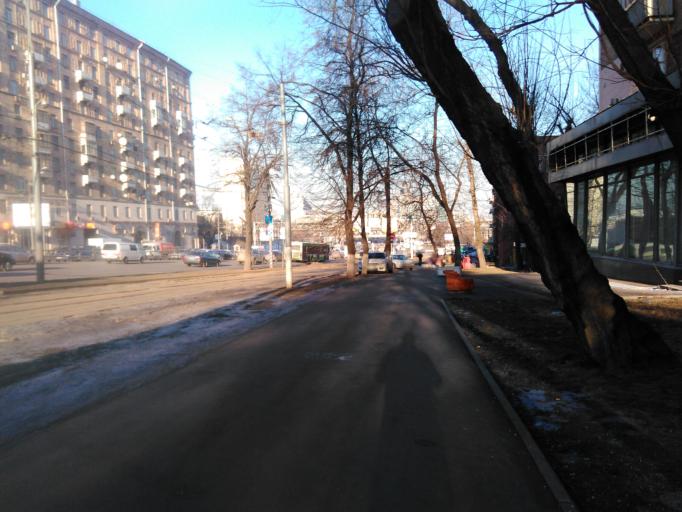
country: RU
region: Moscow
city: Zamoskvorech'ye
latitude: 55.6993
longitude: 37.6209
